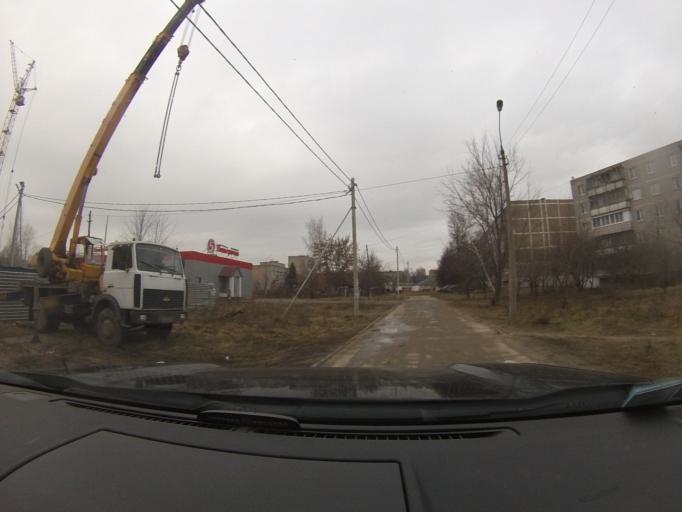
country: RU
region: Moskovskaya
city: Peski
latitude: 55.2730
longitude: 38.7512
